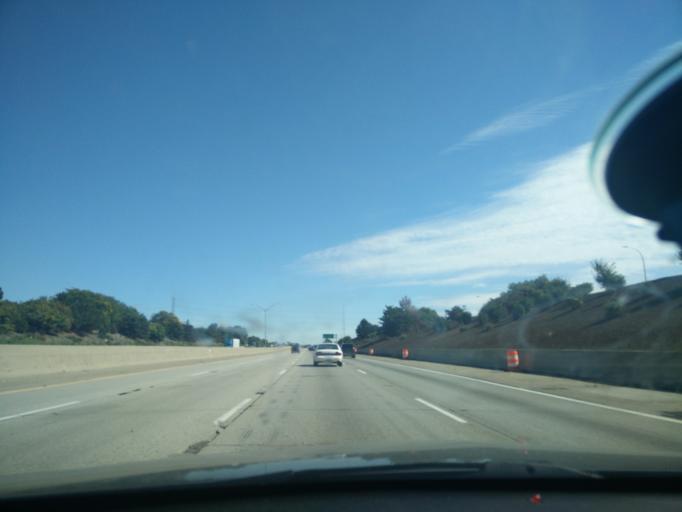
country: US
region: Michigan
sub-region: Macomb County
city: Eastpointe
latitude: 42.4925
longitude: -82.9864
